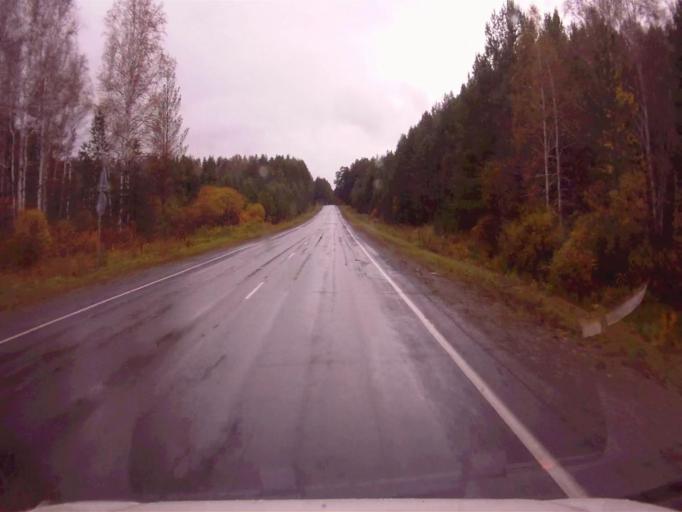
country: RU
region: Chelyabinsk
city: Verkhniy Ufaley
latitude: 56.0189
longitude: 60.3053
